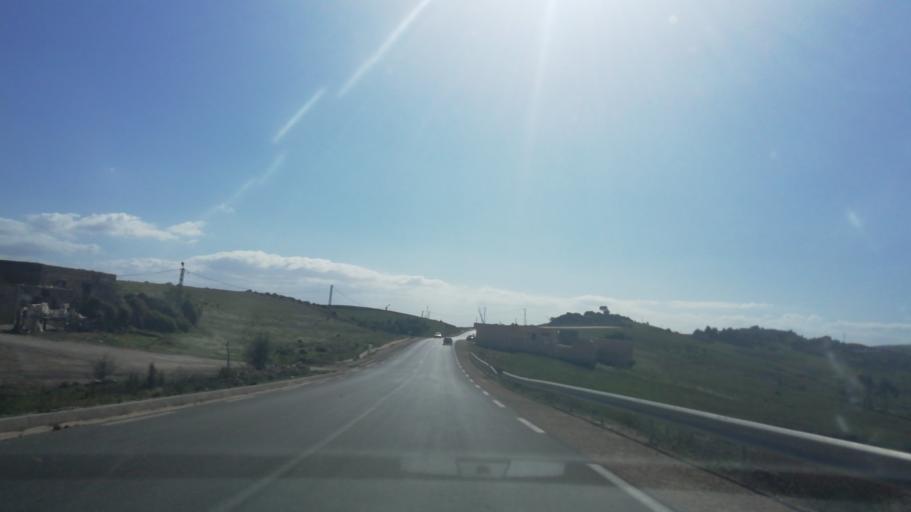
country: DZ
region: Relizane
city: Djidiouia
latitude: 36.0904
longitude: 0.5157
